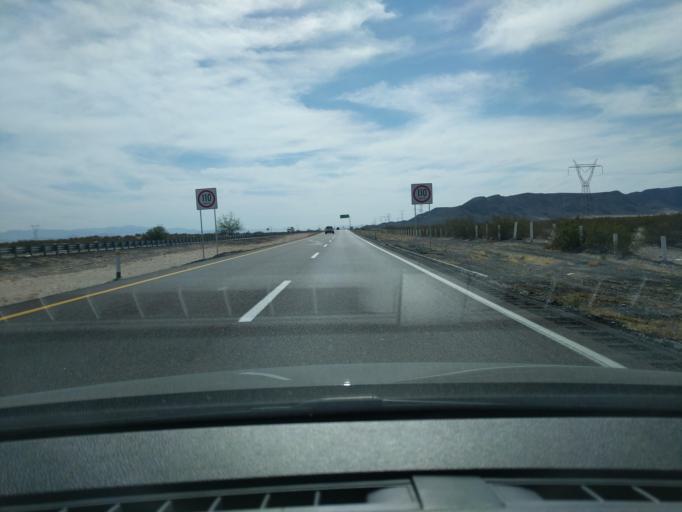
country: MX
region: Coahuila
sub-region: San Pedro
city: San Marcos
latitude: 25.5566
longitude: -103.0317
